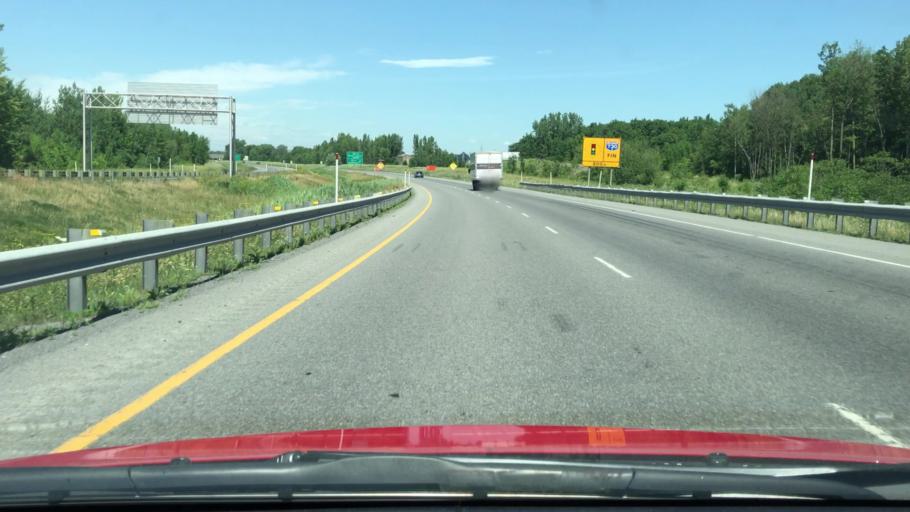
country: CA
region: Quebec
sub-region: Monteregie
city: Saint-Constant
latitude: 45.3880
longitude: -73.6057
